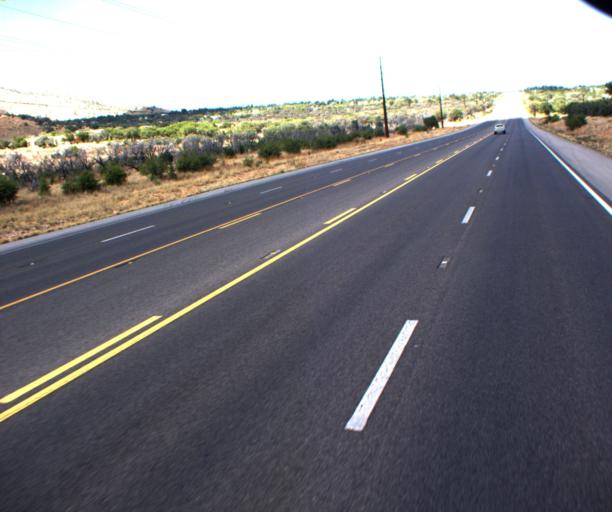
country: US
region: Arizona
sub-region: Cochise County
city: Sierra Vista Southeast
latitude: 31.4116
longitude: -110.2407
